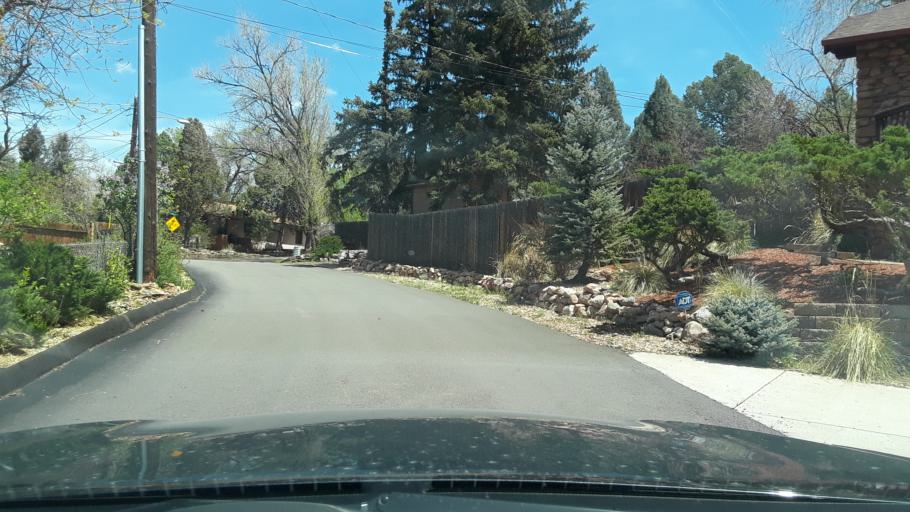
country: US
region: Colorado
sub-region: El Paso County
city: Manitou Springs
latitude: 38.8610
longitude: -104.8843
